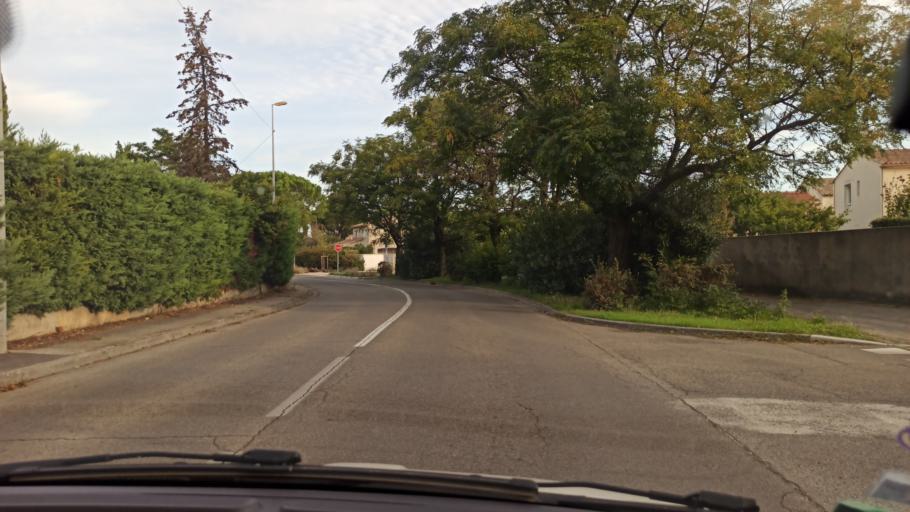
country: FR
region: Provence-Alpes-Cote d'Azur
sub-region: Departement du Vaucluse
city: Le Pontet
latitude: 43.9426
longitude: 4.8489
